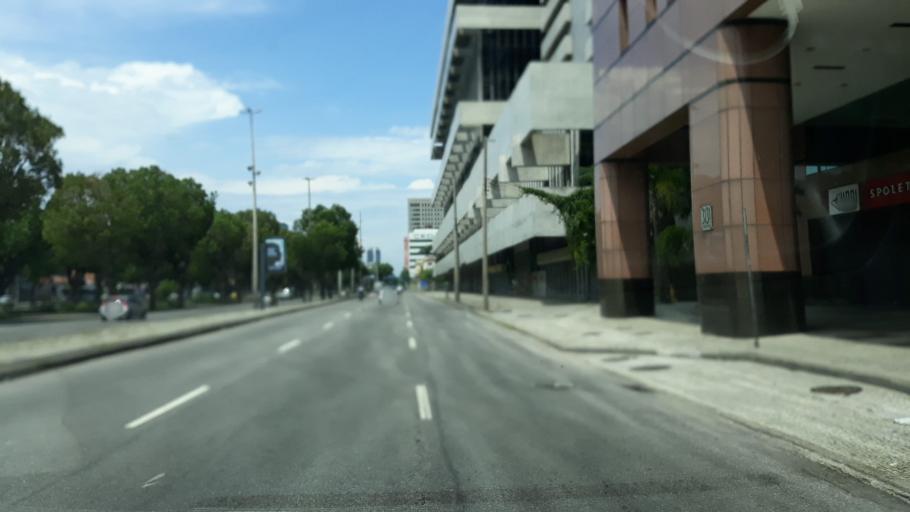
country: BR
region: Rio de Janeiro
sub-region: Rio De Janeiro
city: Rio de Janeiro
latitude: -22.9099
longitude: -43.2045
